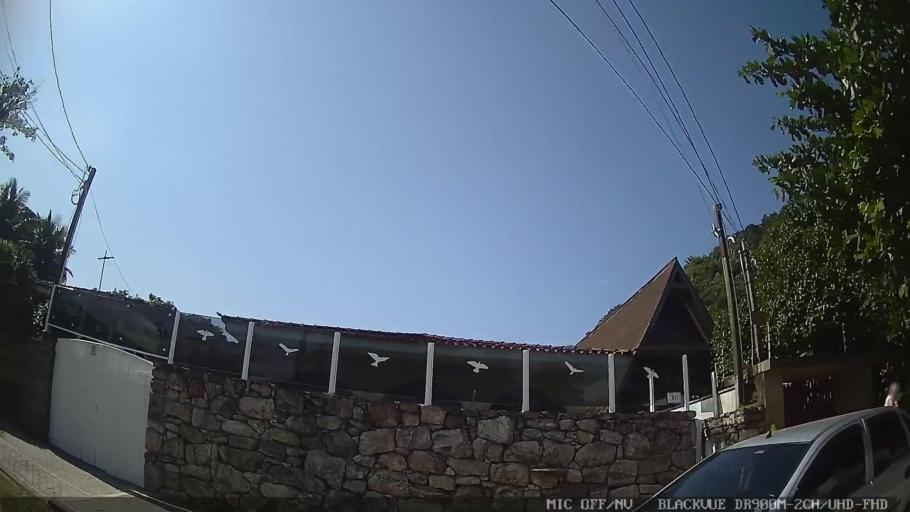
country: BR
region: Sao Paulo
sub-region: Guaruja
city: Guaruja
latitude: -24.0161
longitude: -46.2841
